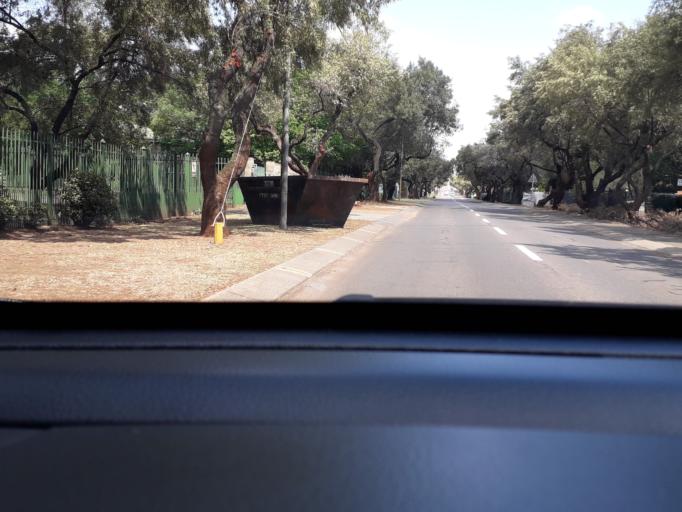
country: ZA
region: Gauteng
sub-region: City of Tshwane Metropolitan Municipality
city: Centurion
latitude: -25.8347
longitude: 28.2127
